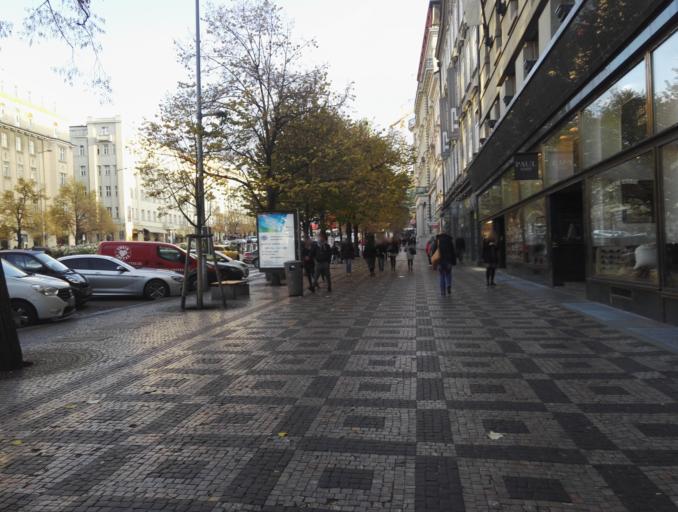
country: CZ
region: Praha
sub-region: Praha 1
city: Stare Mesto
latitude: 50.0811
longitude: 14.4274
